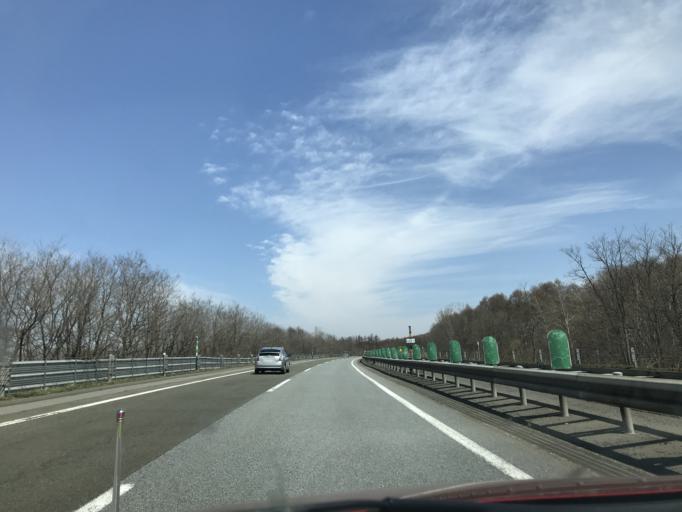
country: JP
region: Hokkaido
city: Bibai
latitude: 43.2926
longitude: 141.8659
